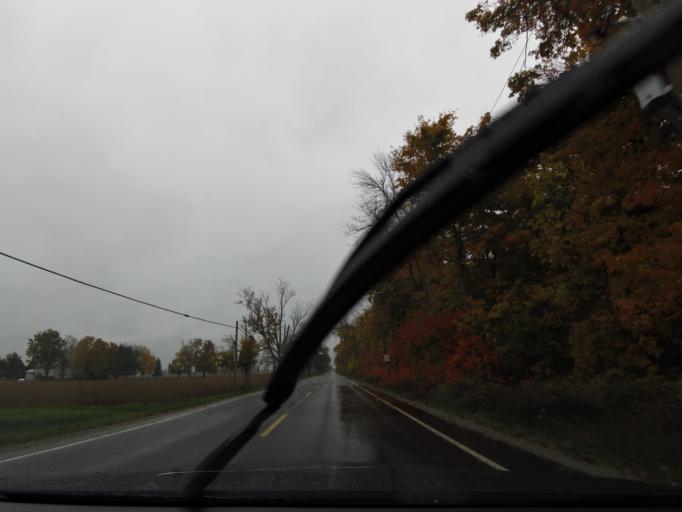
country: CA
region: Ontario
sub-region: Halton
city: Milton
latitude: 43.4591
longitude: -79.8940
